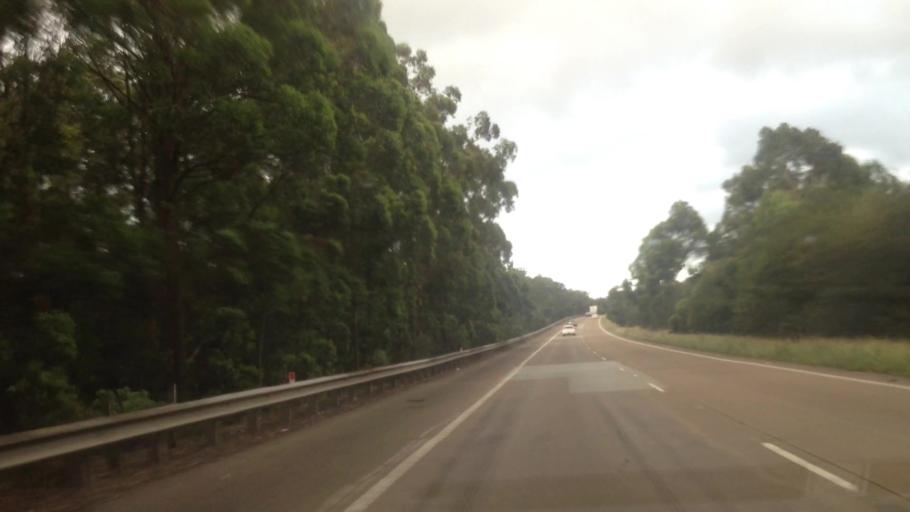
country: AU
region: New South Wales
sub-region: Wyong Shire
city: Charmhaven
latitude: -33.1565
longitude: 151.4704
